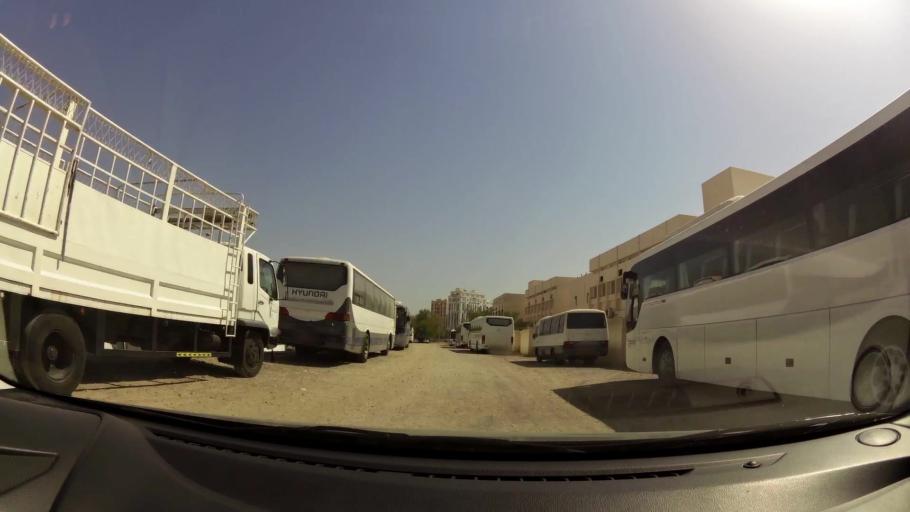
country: OM
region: Muhafazat Masqat
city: Muscat
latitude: 23.5981
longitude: 58.5446
